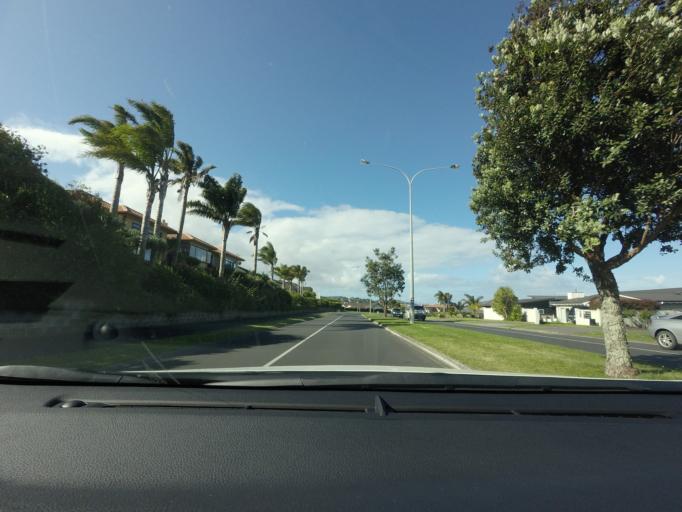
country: NZ
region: Auckland
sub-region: Auckland
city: Rothesay Bay
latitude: -36.5862
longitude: 174.6826
